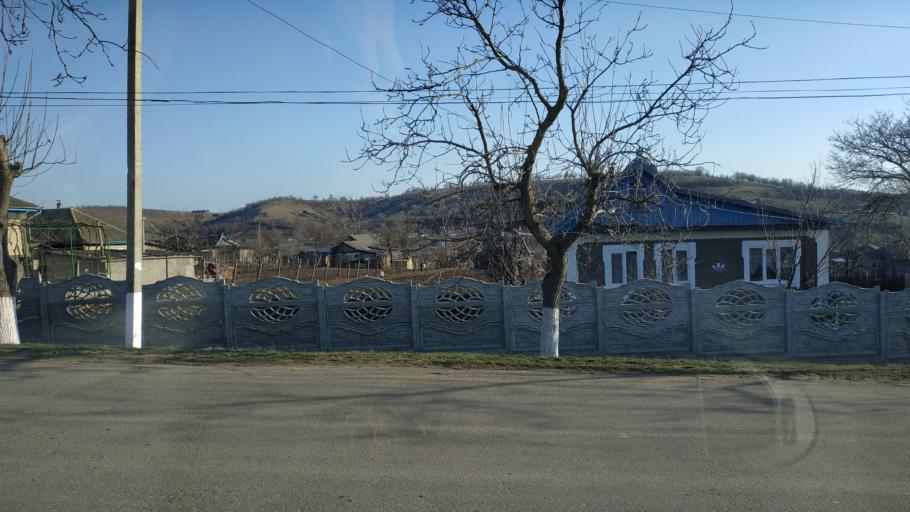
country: MD
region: Hincesti
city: Hincesti
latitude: 46.7028
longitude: 28.5309
